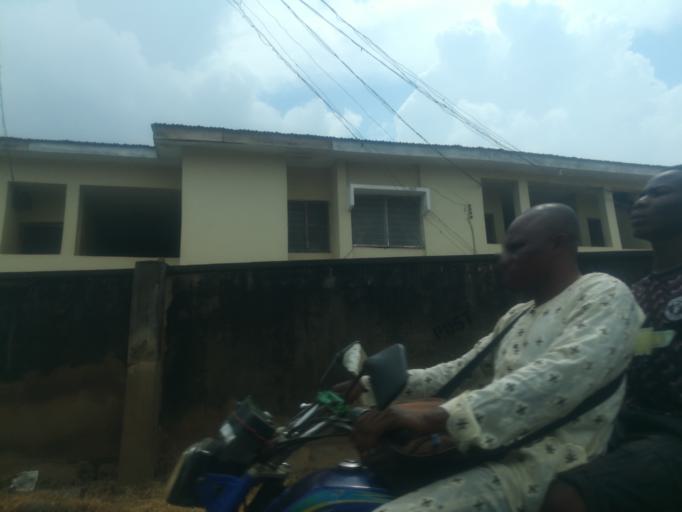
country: NG
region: Oyo
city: Ibadan
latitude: 7.4301
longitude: 3.9157
